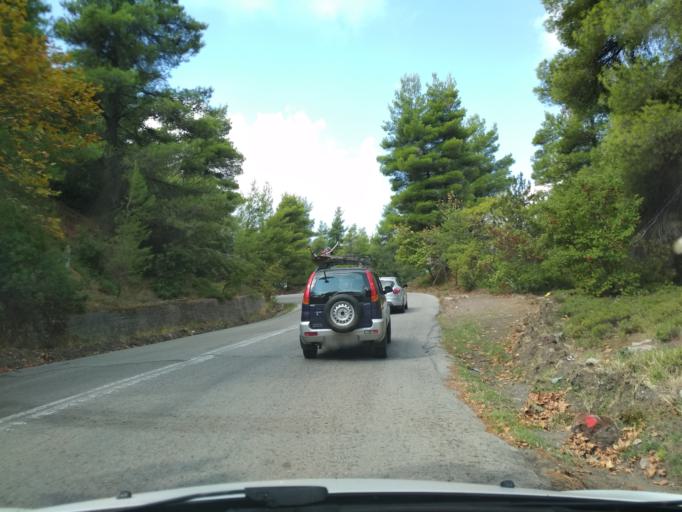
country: GR
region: Central Greece
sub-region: Nomos Evvoias
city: Politika
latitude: 38.6712
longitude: 23.5593
